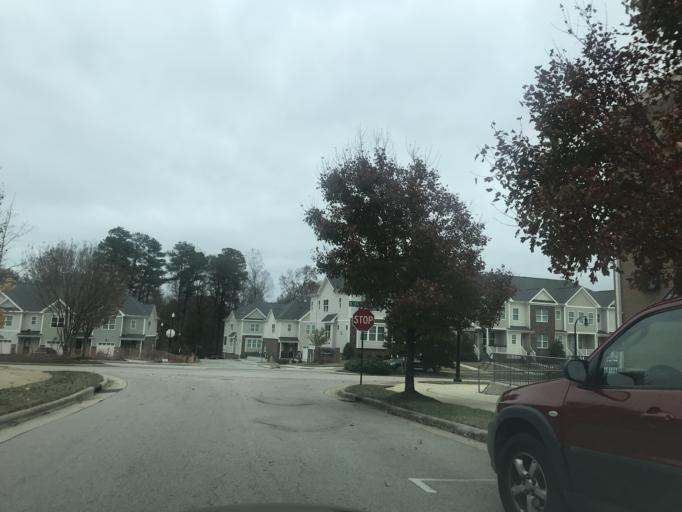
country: US
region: North Carolina
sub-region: Wake County
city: Wake Forest
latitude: 35.9665
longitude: -78.5111
